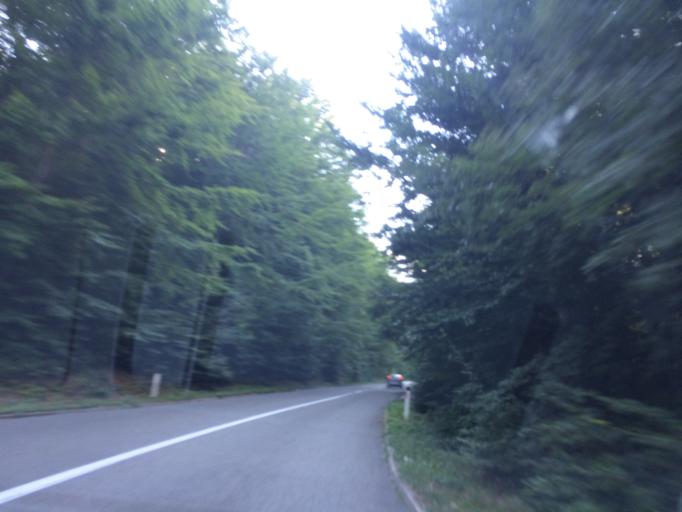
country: ME
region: Opstina Savnik
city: Savnik
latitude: 42.9475
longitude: 19.0979
